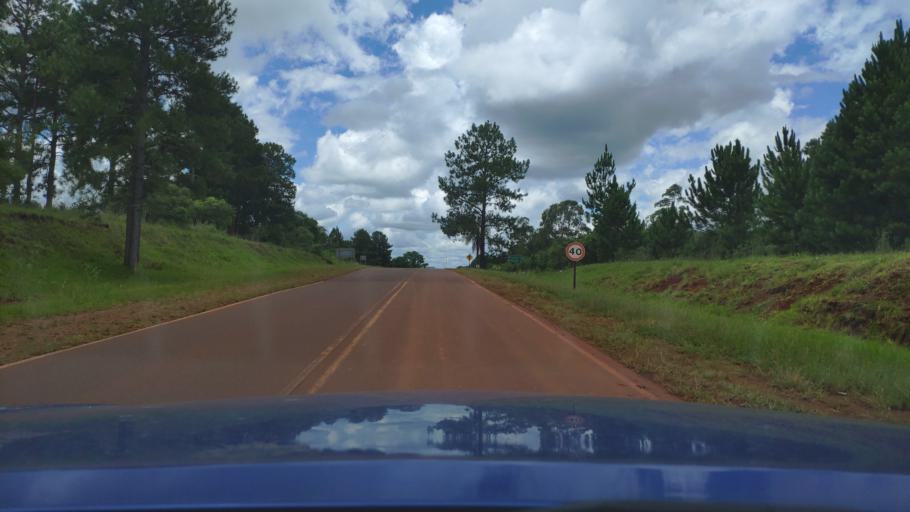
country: AR
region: Misiones
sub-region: Departamento de San Javier
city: San Javier
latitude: -27.8393
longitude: -55.2220
